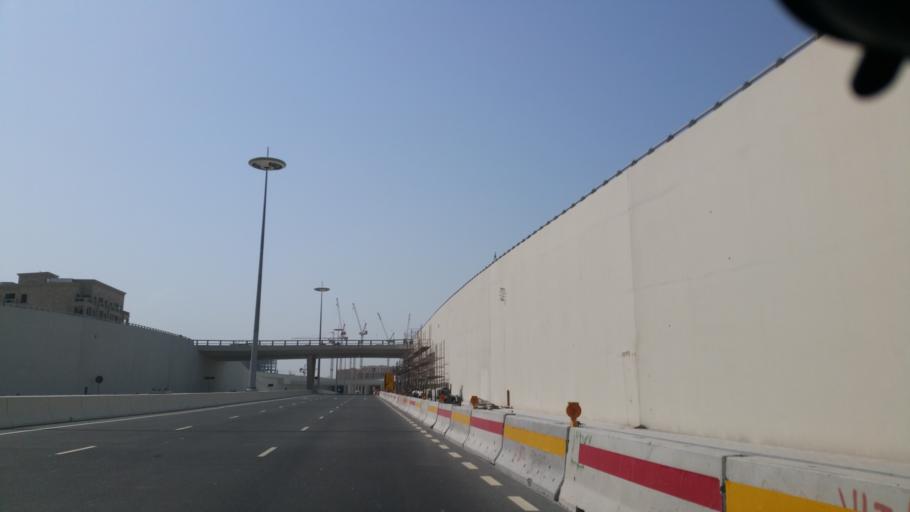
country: QA
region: Baladiyat Umm Salal
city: Umm Salal Muhammad
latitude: 25.4107
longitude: 51.5103
